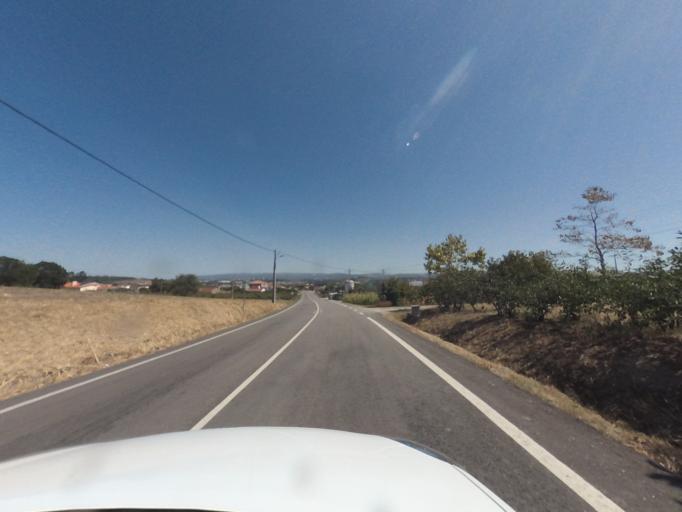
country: PT
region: Leiria
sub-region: Alcobaca
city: Alcobaca
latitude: 39.5200
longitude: -9.0271
